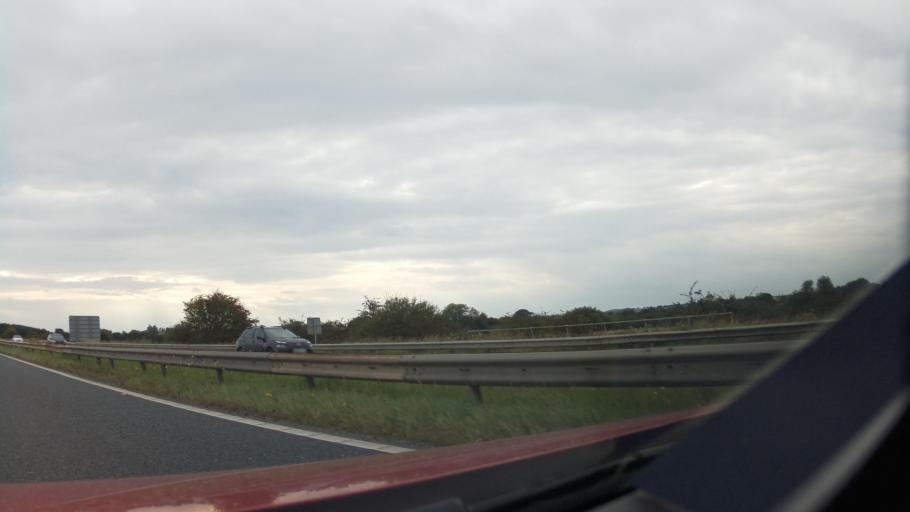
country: GB
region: England
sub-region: Darlington
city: Coatham Mundeville
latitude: 54.5691
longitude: -1.5796
